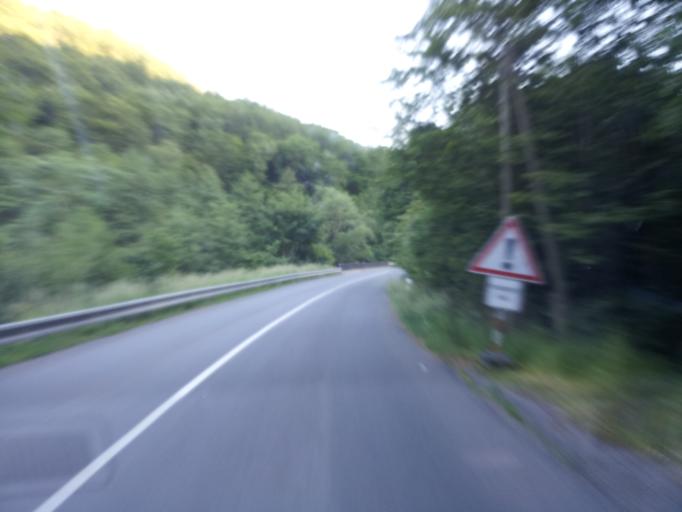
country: SK
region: Banskobystricky
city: Krupina
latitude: 48.3273
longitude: 18.9778
